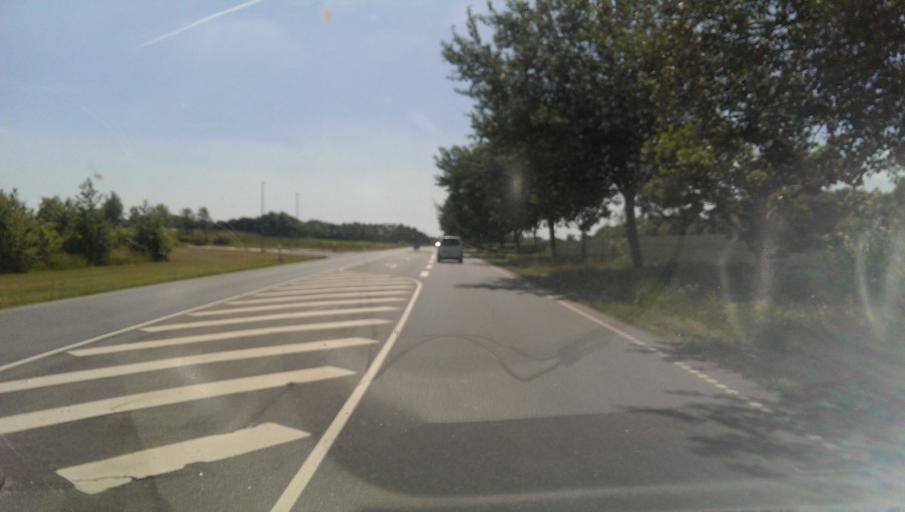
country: DK
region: South Denmark
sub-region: Esbjerg Kommune
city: Esbjerg
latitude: 55.5342
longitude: 8.4151
